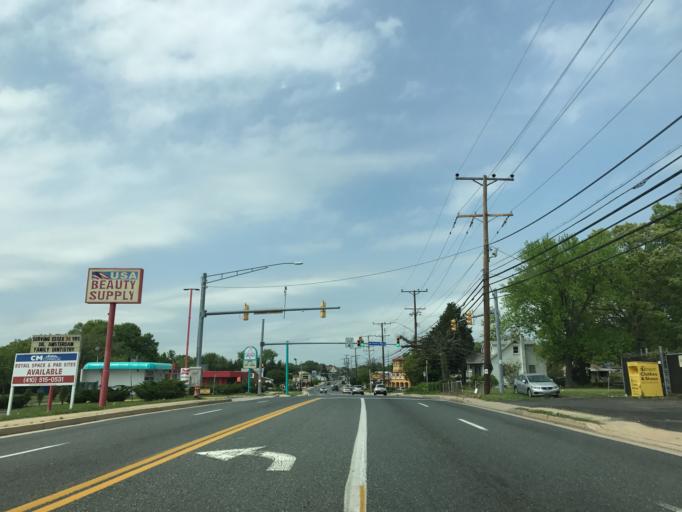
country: US
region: Maryland
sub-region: Baltimore County
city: Middle River
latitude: 39.3102
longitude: -76.4462
